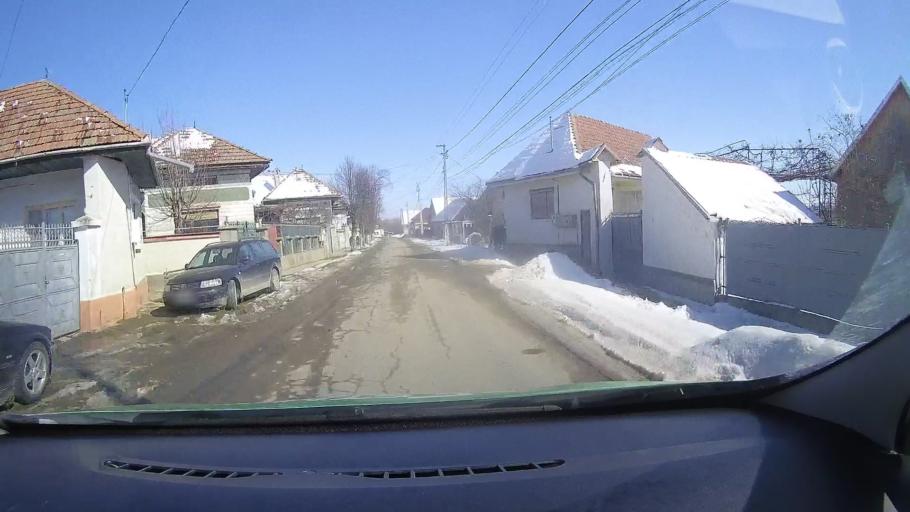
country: RO
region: Brasov
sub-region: Comuna Mandra
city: Mandra
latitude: 45.8227
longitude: 25.0066
